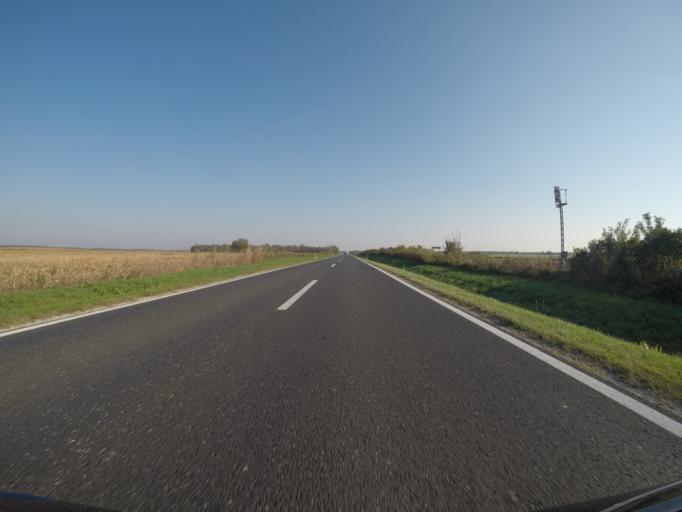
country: HR
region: Koprivnicko-Krizevacka
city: Kalinovac
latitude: 46.0088
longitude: 17.1028
